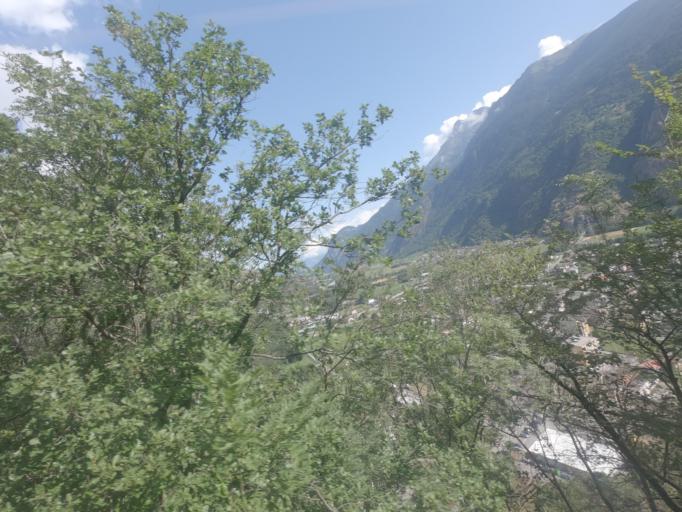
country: CH
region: Valais
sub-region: Saint-Maurice District
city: Vernayaz
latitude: 46.1324
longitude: 7.0363
